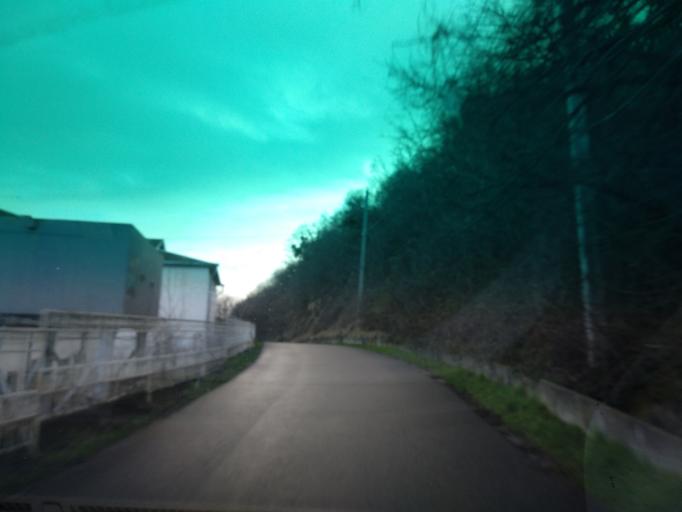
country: RU
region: Krasnodarskiy
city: Novomikhaylovskiy
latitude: 44.2439
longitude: 38.8340
